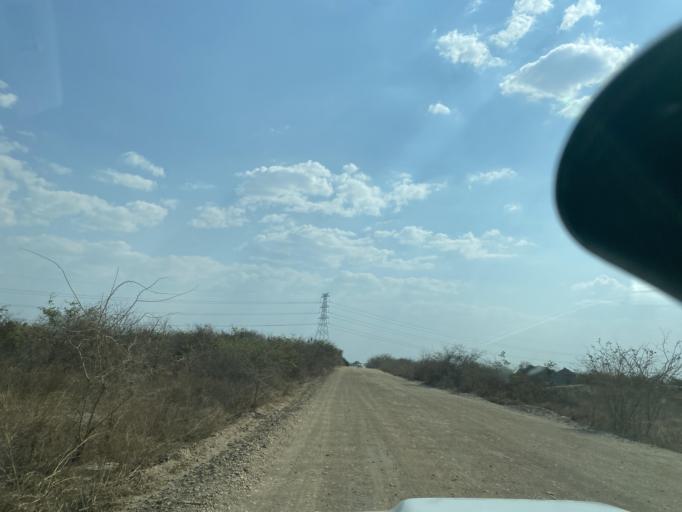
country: ZM
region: Lusaka
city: Lusaka
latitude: -15.3671
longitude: 28.0848
